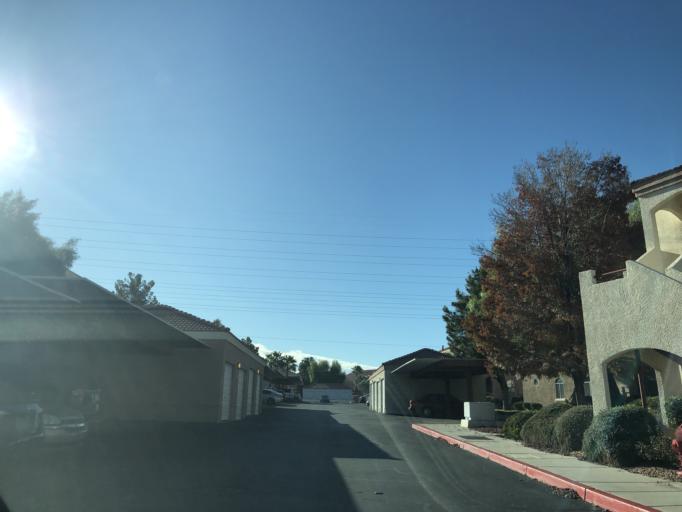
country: US
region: Nevada
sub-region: Clark County
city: Whitney
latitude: 36.0035
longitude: -115.0937
